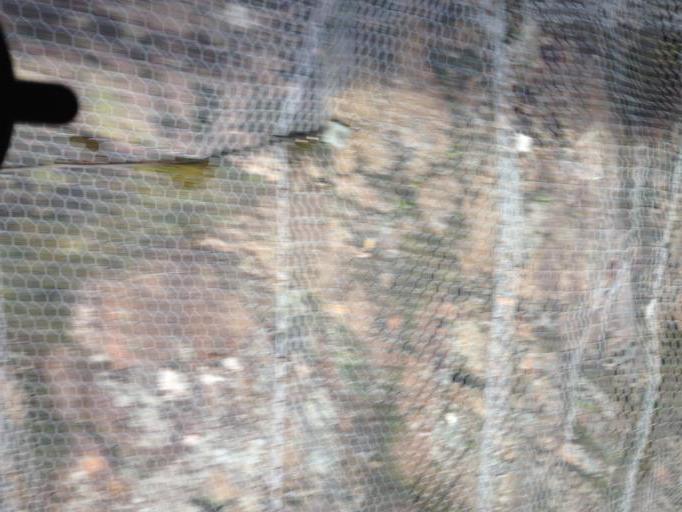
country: GB
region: Scotland
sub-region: Argyll and Bute
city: Garelochhead
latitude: 56.1659
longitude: -4.7822
